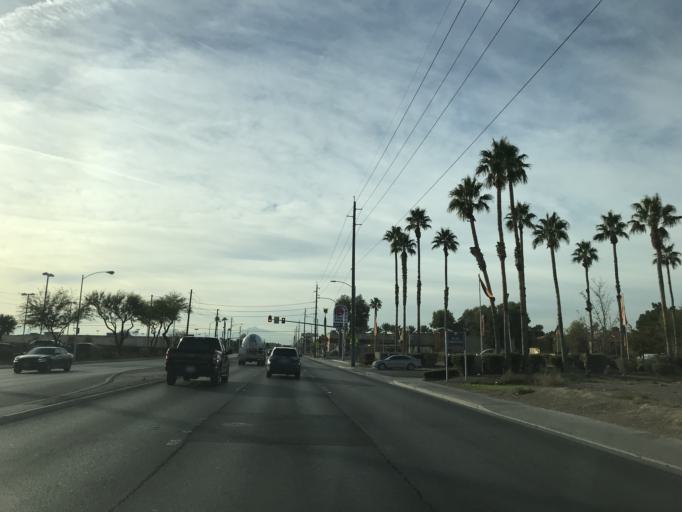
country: US
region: Nevada
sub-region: Clark County
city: Sunrise Manor
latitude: 36.1717
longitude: -115.0622
